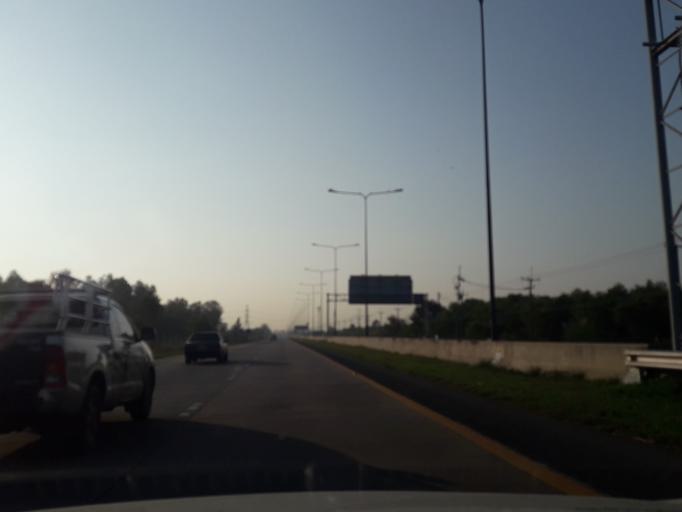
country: TH
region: Pathum Thani
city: Sam Khok
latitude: 14.1414
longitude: 100.5598
